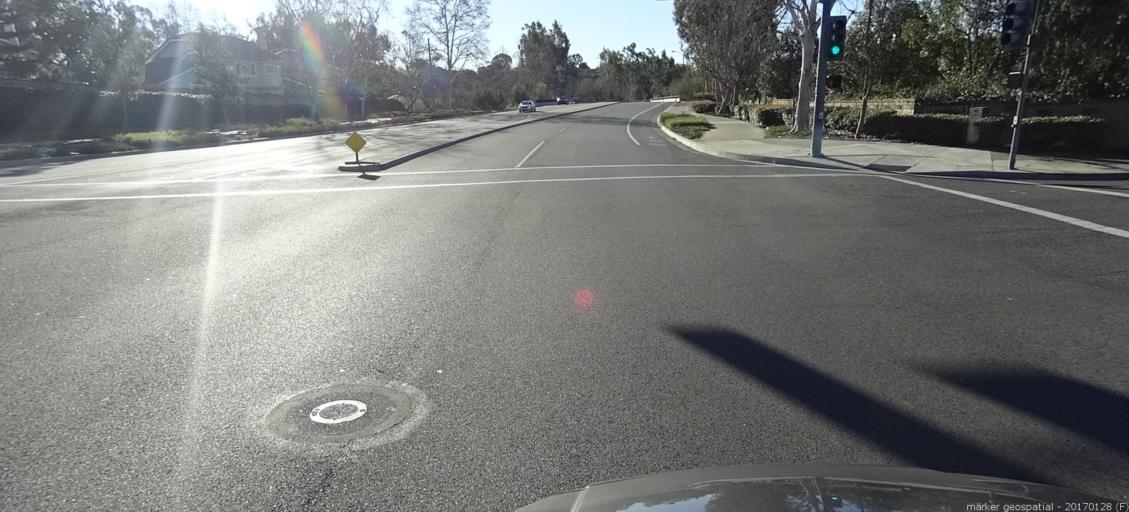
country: US
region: California
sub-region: Orange County
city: Lake Forest
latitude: 33.6348
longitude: -117.6777
